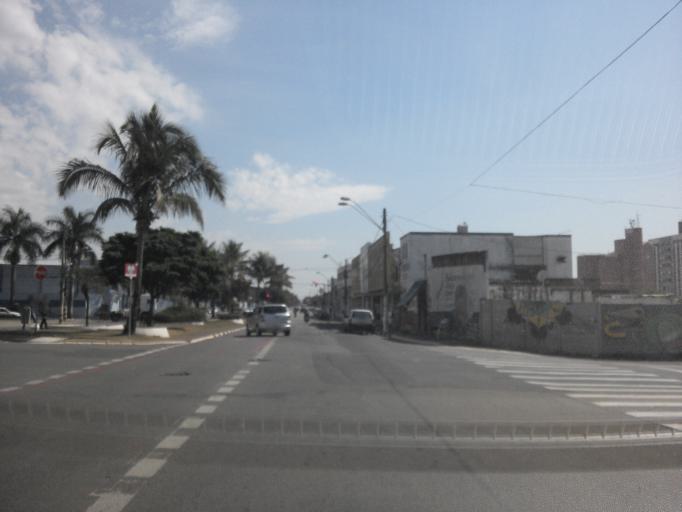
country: BR
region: Sao Paulo
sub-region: Sumare
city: Sumare
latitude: -22.8272
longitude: -47.2682
